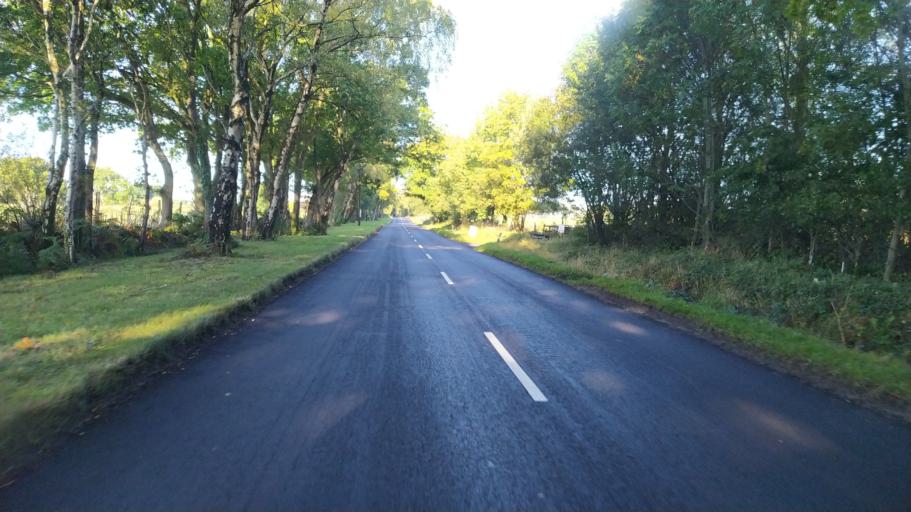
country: GB
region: England
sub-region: Dorset
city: Three Legged Cross
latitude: 50.8543
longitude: -1.9027
